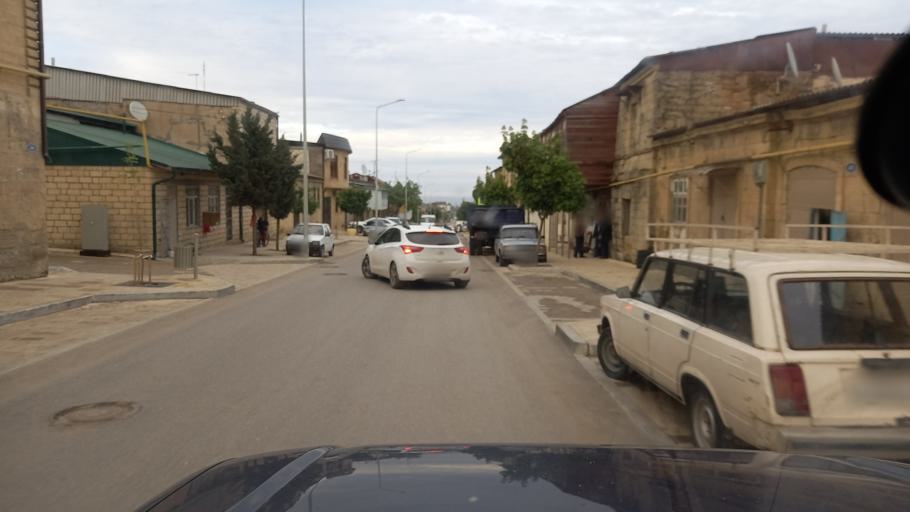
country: RU
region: Dagestan
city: Derbent
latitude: 42.0565
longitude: 48.2835
